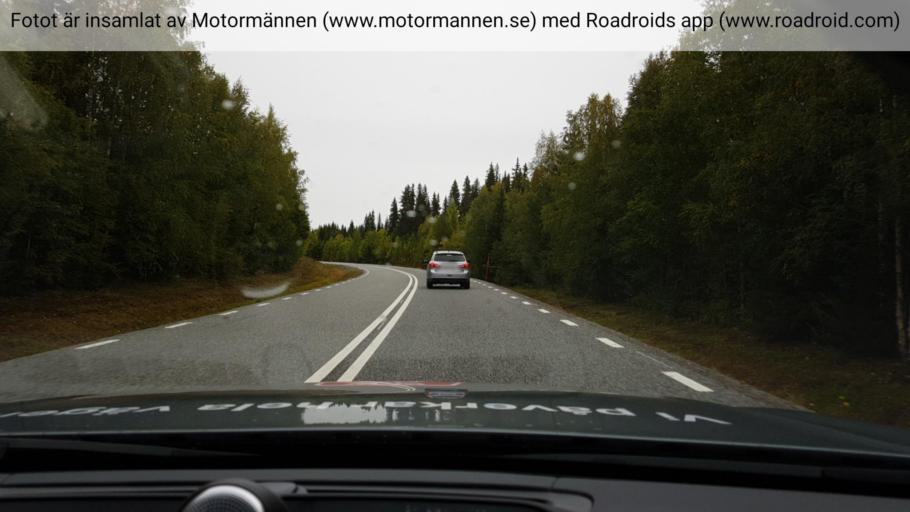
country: SE
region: Jaemtland
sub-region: Stroemsunds Kommun
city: Stroemsund
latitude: 64.0707
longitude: 15.5599
